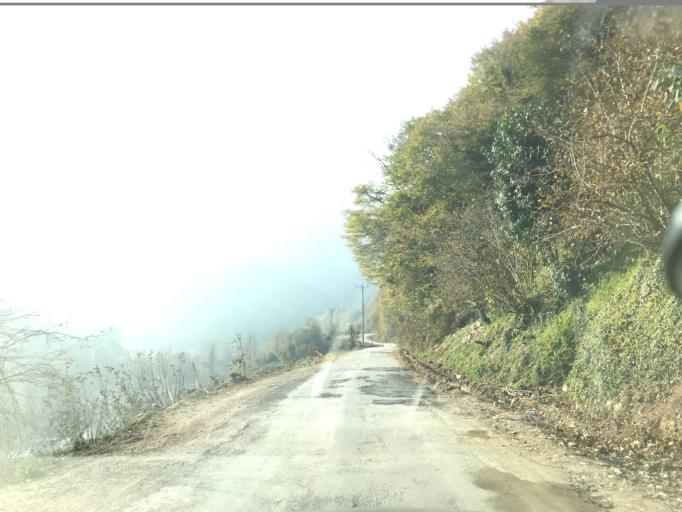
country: TR
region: Duzce
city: Cumayeri
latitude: 40.9341
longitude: 30.9272
